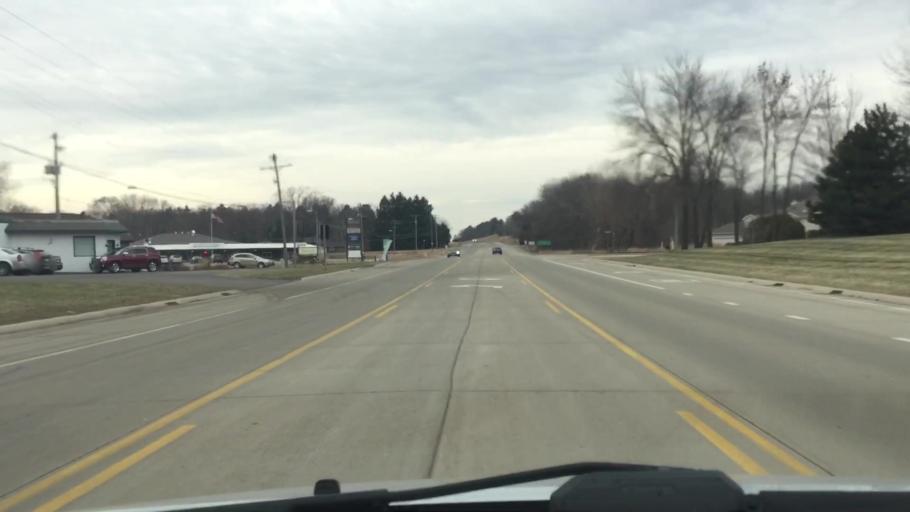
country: US
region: Wisconsin
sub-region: Waukesha County
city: Oconomowoc
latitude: 43.1273
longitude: -88.5357
